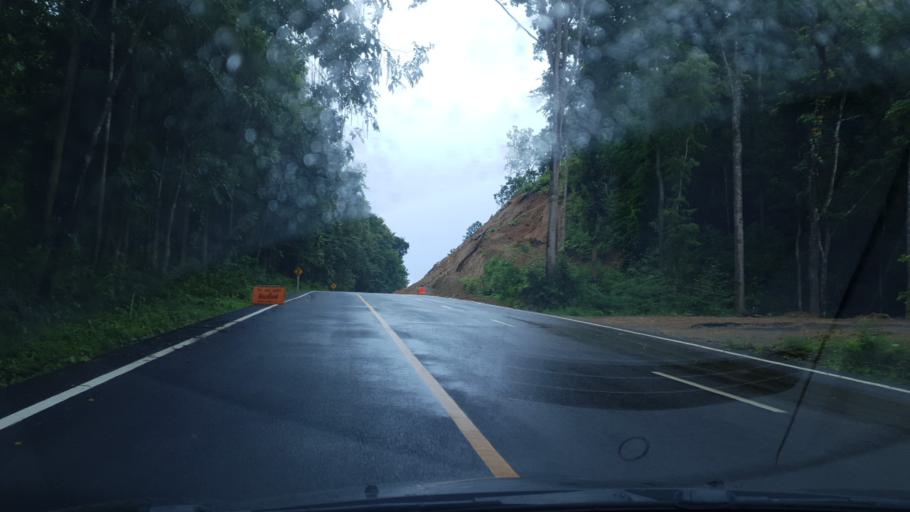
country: TH
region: Mae Hong Son
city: Pa Pae
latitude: 18.2664
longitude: 97.9427
